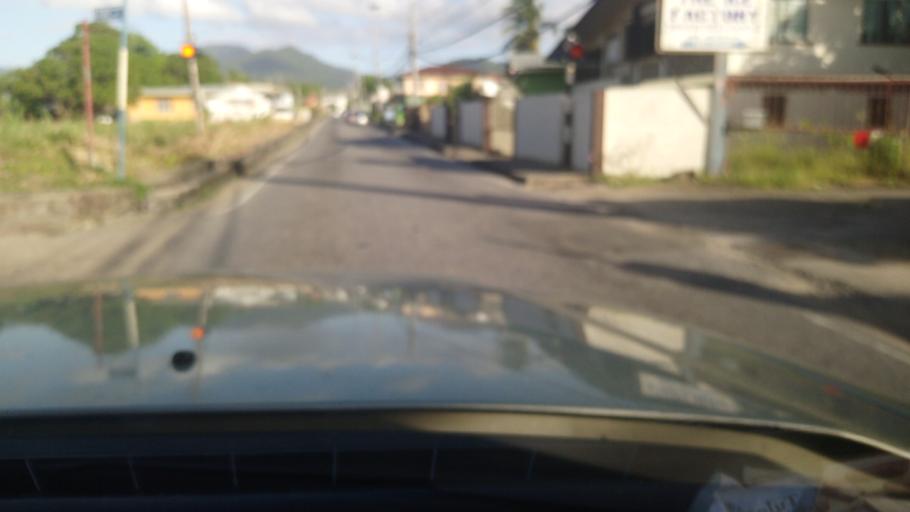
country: TT
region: Borough of Arima
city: Arima
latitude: 10.6276
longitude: -61.2744
